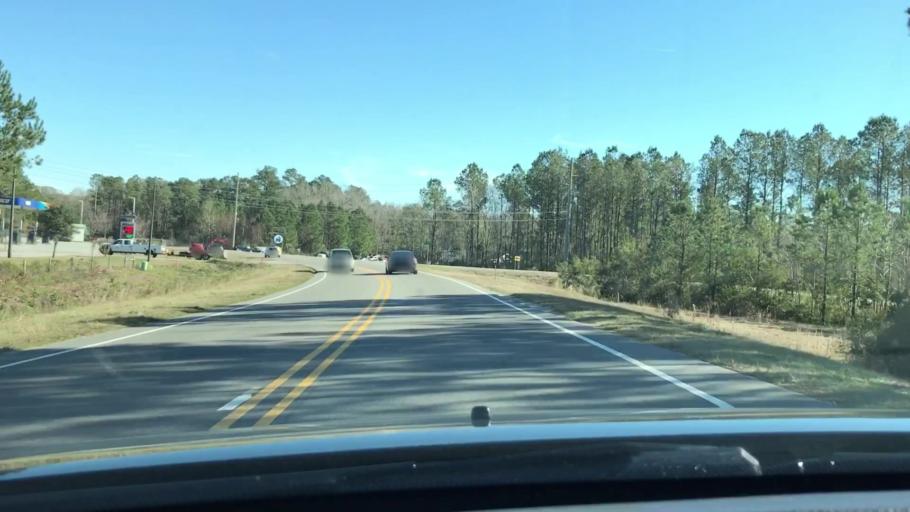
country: US
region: North Carolina
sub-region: Brunswick County
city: Shallotte
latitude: 33.9603
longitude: -78.4165
